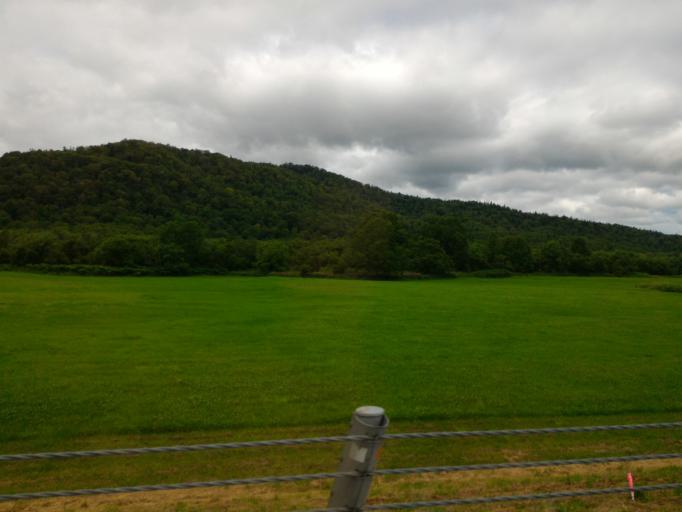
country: JP
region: Hokkaido
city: Nayoro
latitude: 44.7239
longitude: 142.2510
